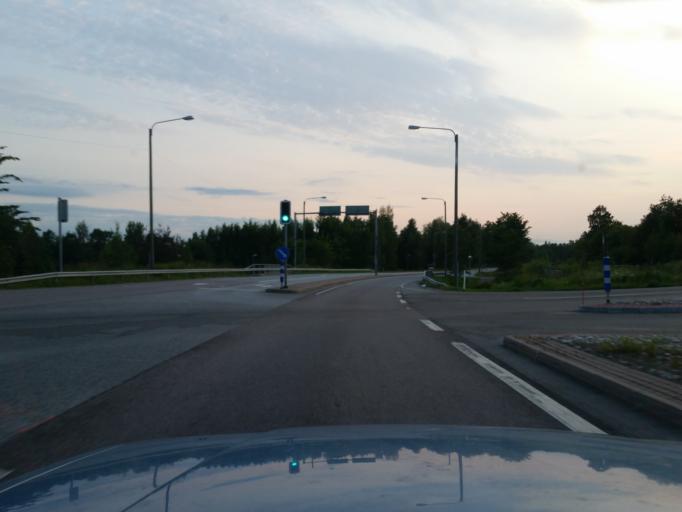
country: FI
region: Southern Savonia
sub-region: Savonlinna
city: Savonlinna
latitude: 61.8777
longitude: 28.8204
